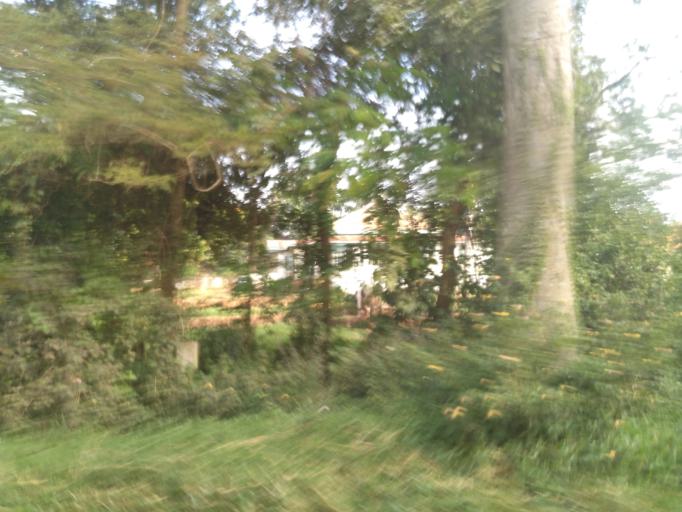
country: UG
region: Eastern Region
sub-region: Jinja District
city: Jinja
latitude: 0.4225
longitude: 33.2004
